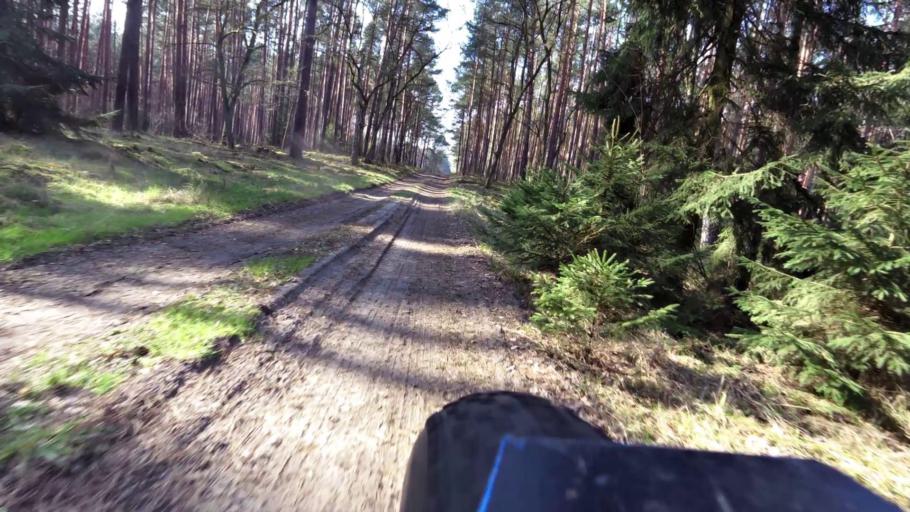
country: PL
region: Lubusz
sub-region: Powiat slubicki
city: Cybinka
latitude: 52.2390
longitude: 14.8008
